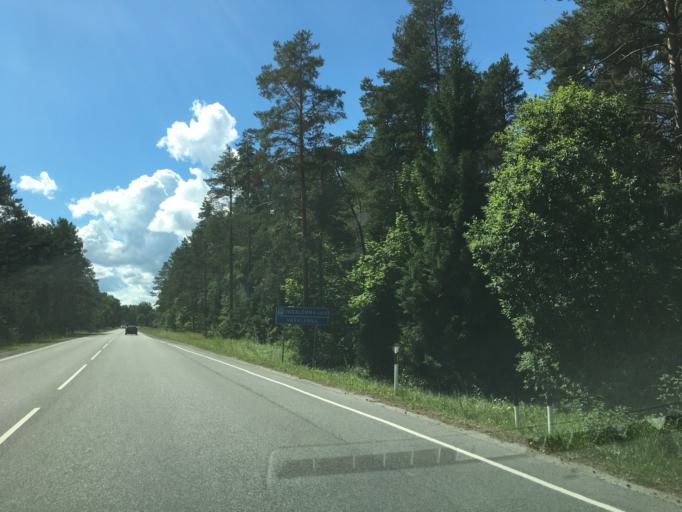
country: EE
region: Harju
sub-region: Nissi vald
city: Riisipere
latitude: 59.2440
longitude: 24.2779
